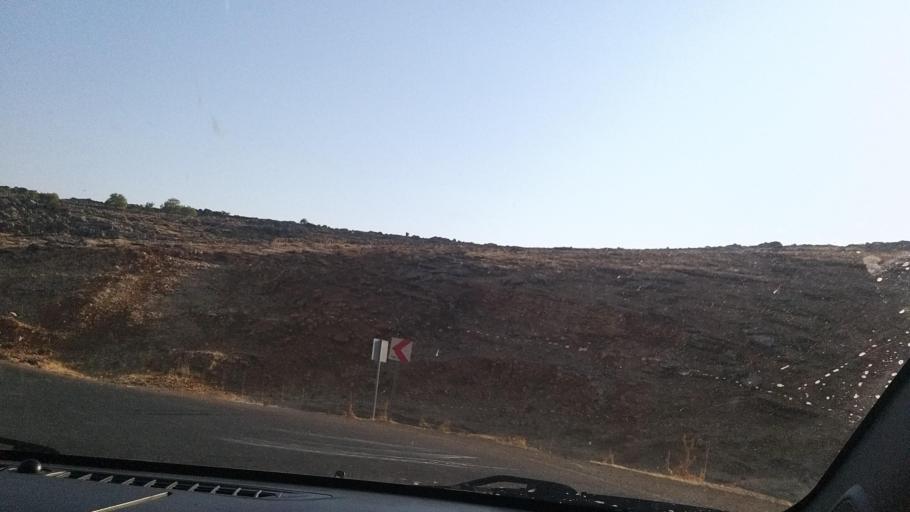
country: TR
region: Diyarbakir
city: Silvan
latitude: 38.1692
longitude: 41.0013
